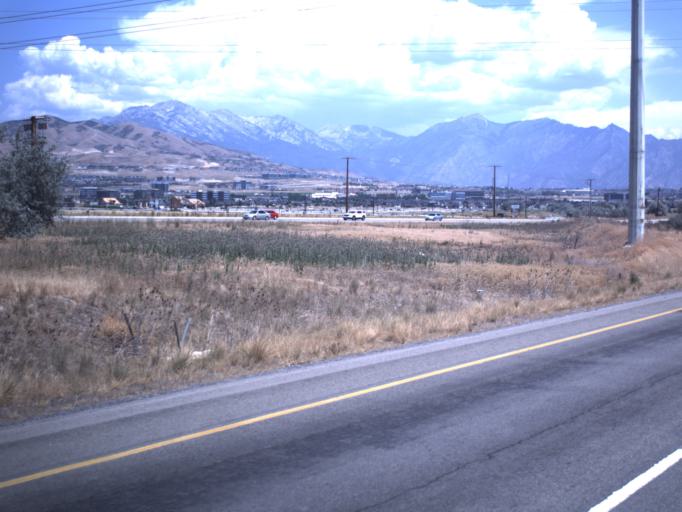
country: US
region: Utah
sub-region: Utah County
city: Lehi
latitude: 40.4125
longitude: -111.9095
